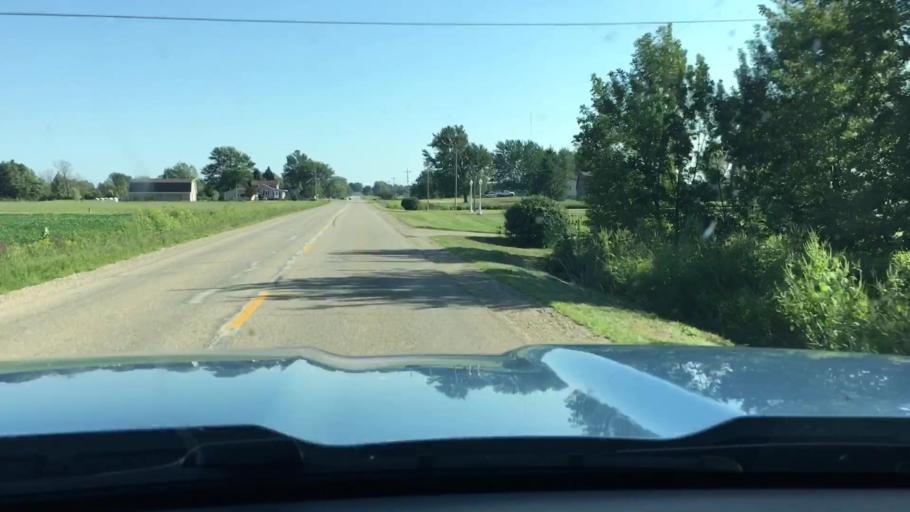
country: US
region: Michigan
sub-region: Ottawa County
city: Zeeland
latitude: 42.8697
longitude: -85.9604
